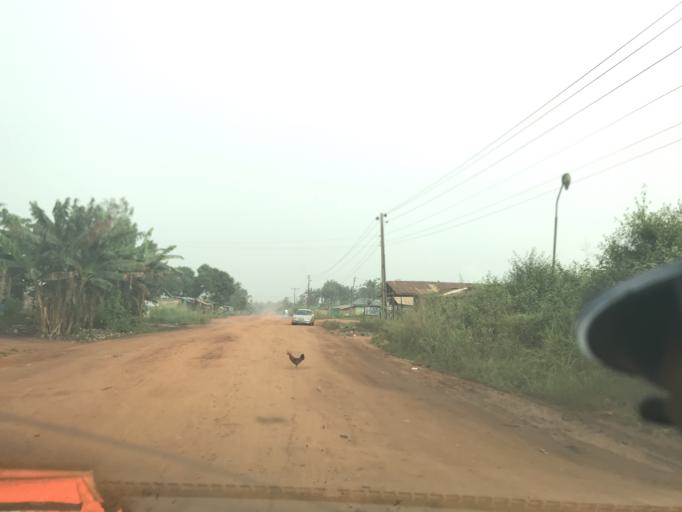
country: NG
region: Ogun
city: Ado Odo
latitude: 6.5378
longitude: 2.9499
